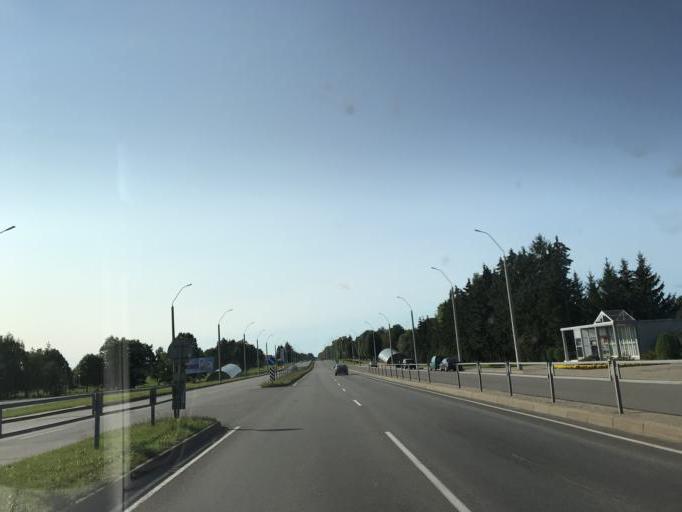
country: BY
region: Mogilev
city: Buynichy
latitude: 53.8632
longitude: 30.2590
